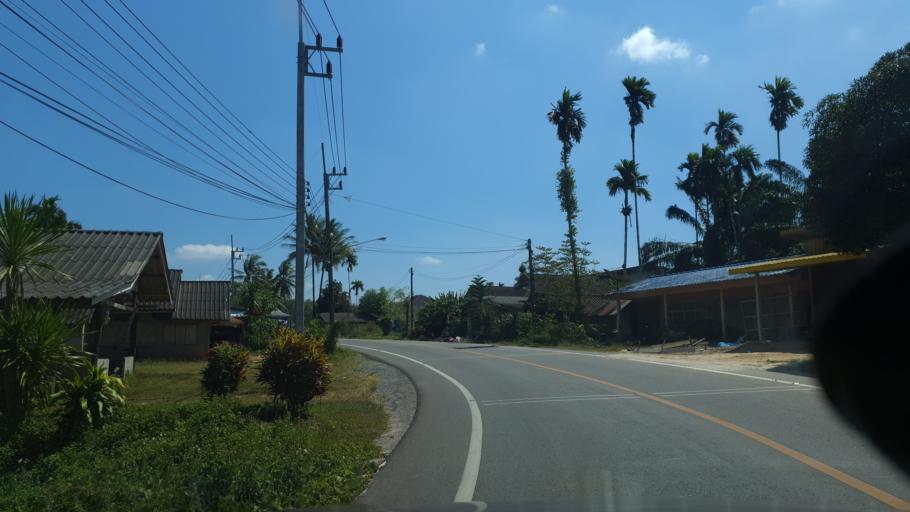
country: TH
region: Krabi
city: Khlong Thom
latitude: 7.9225
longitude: 99.2450
